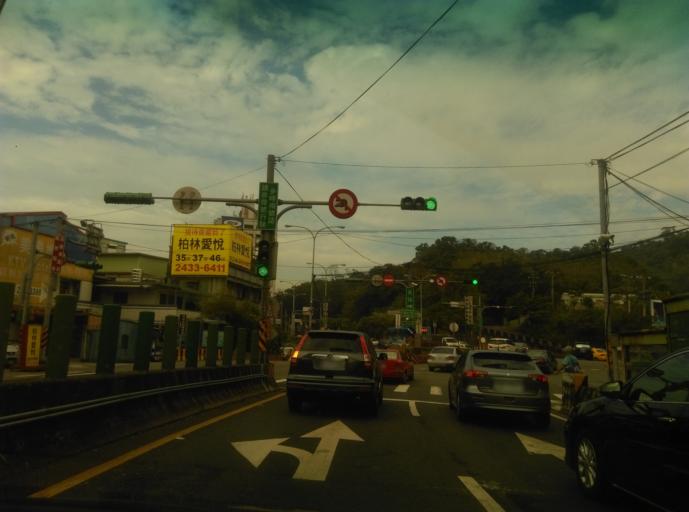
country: TW
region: Taiwan
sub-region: Keelung
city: Keelung
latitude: 25.1417
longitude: 121.7034
